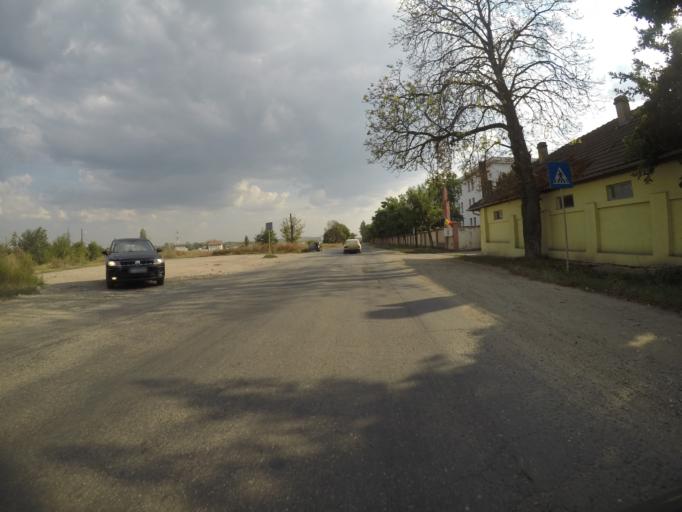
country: RO
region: Cluj
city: Turda
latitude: 46.5470
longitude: 23.7839
